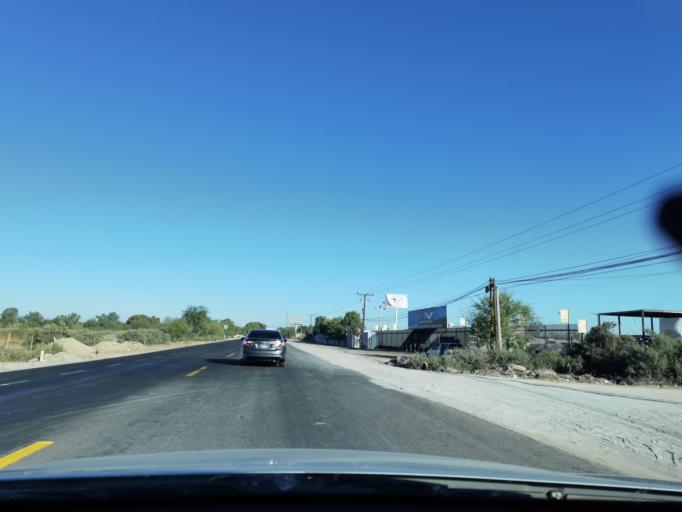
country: MX
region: Baja California
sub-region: Mexicali
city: Islas Agrarias Grupo A
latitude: 32.6483
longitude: -115.3318
